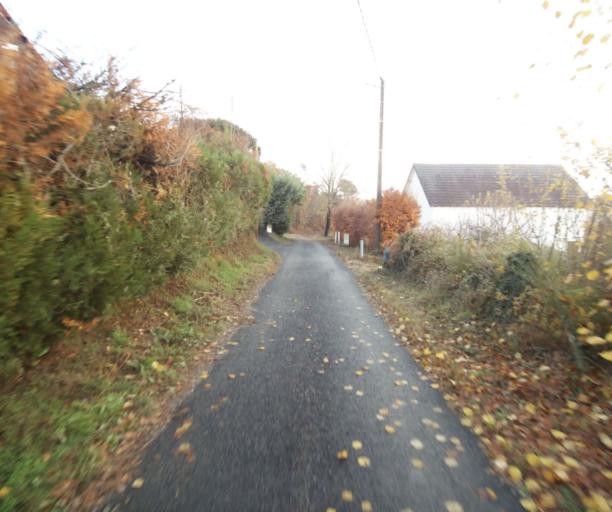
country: FR
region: Limousin
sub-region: Departement de la Correze
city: Cornil
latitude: 45.2164
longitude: 1.6735
